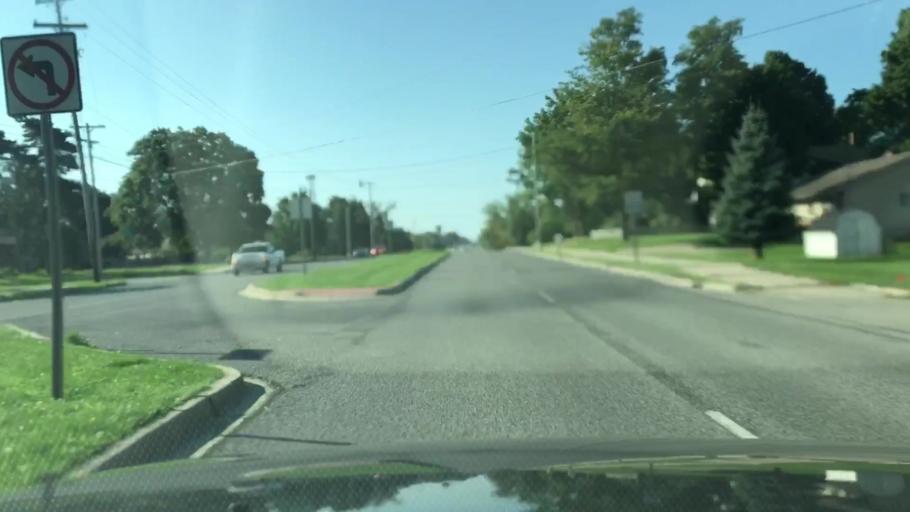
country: US
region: Michigan
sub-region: Kent County
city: Kentwood
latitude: 42.8758
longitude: -85.6257
